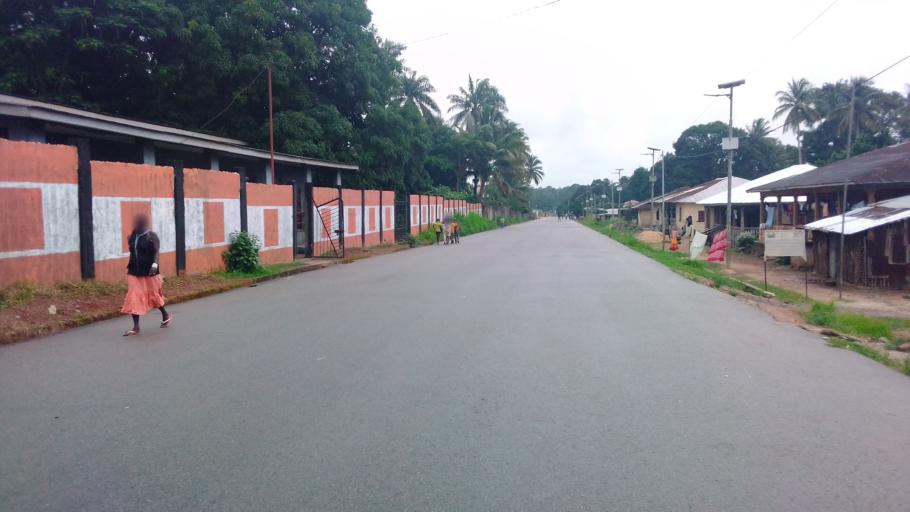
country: SL
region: Northern Province
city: Lunsar
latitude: 8.6843
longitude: -12.5353
